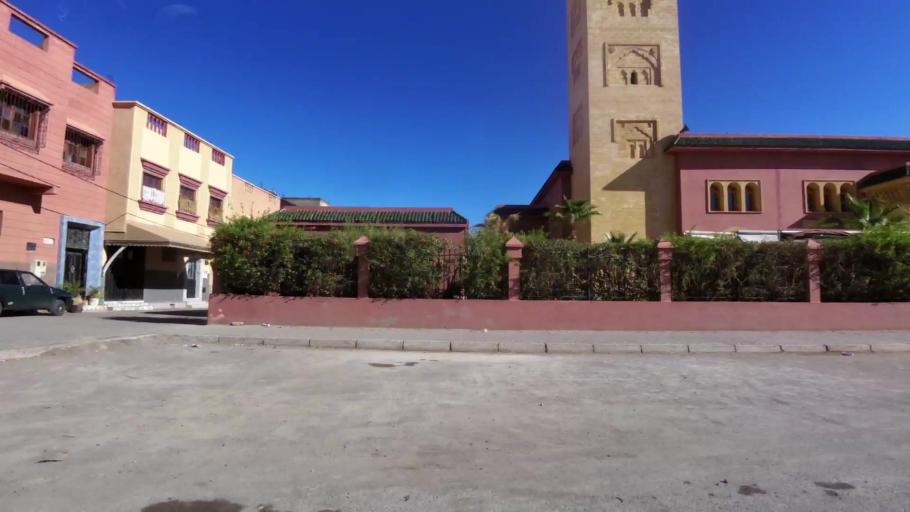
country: MA
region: Marrakech-Tensift-Al Haouz
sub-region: Marrakech
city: Marrakesh
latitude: 31.5909
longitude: -8.0218
